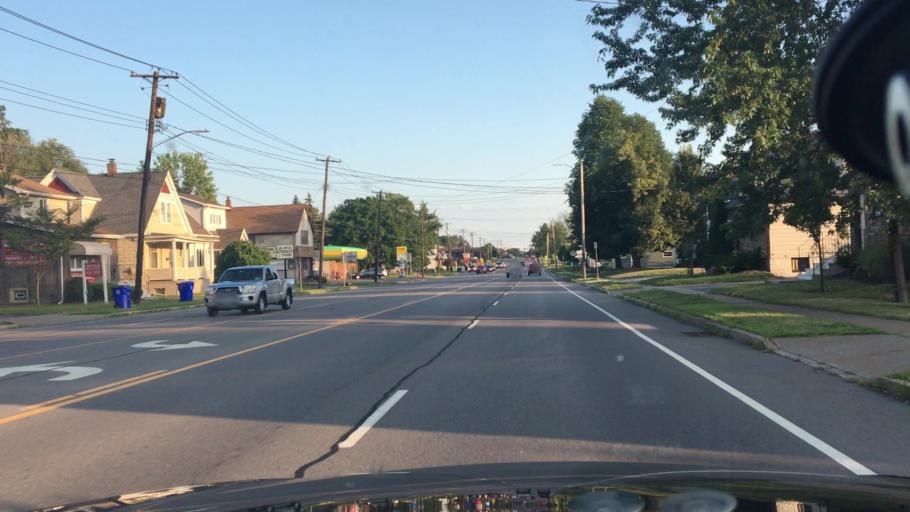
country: US
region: New York
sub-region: Erie County
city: West Seneca
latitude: 42.8388
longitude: -78.7542
